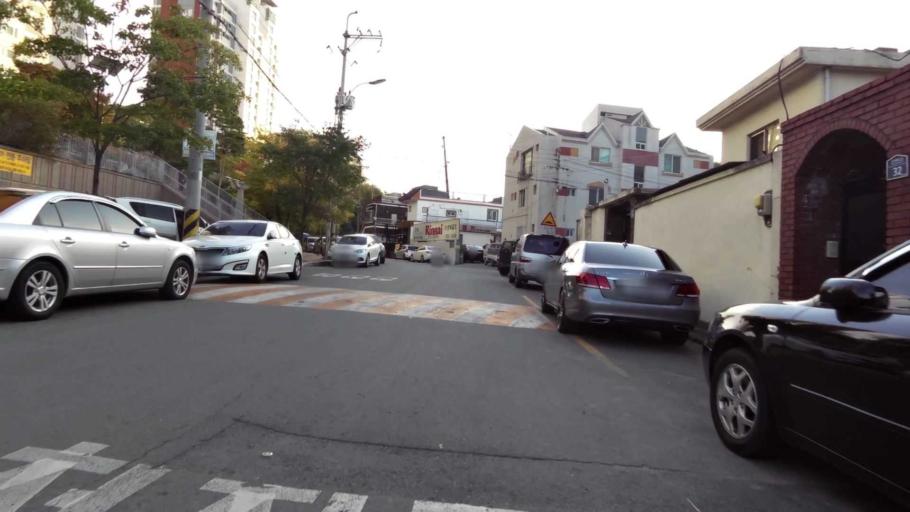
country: KR
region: Daegu
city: Daegu
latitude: 35.8566
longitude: 128.6472
